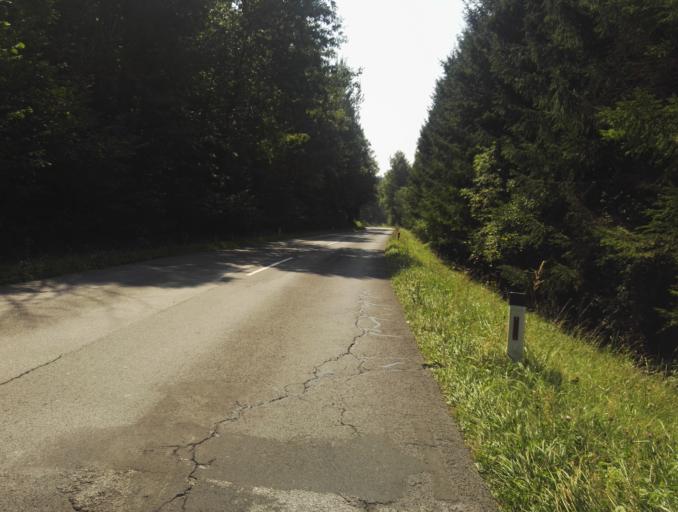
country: AT
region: Styria
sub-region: Politischer Bezirk Graz-Umgebung
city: Gratwein
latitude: 47.1150
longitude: 15.3000
